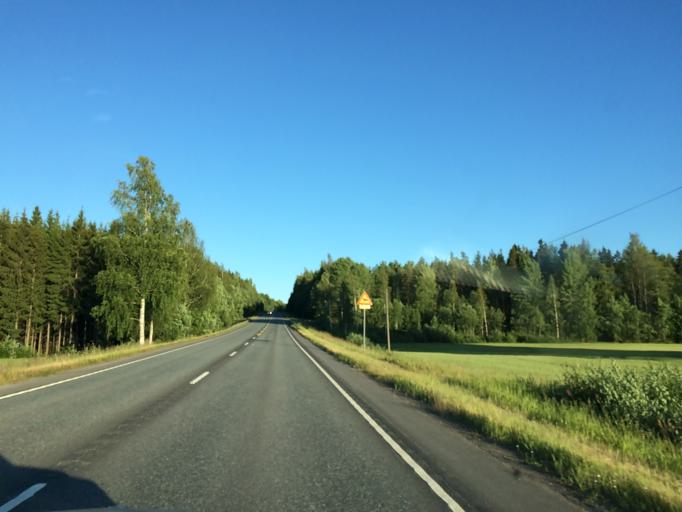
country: FI
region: Haeme
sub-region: Riihimaeki
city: Riihimaeki
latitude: 60.7680
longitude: 24.7076
